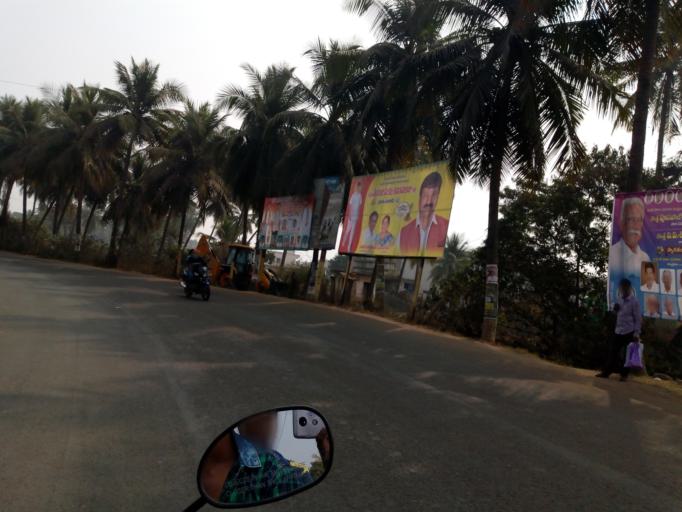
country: IN
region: Andhra Pradesh
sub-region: West Godavari
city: Bhimavaram
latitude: 16.5845
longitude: 81.4677
